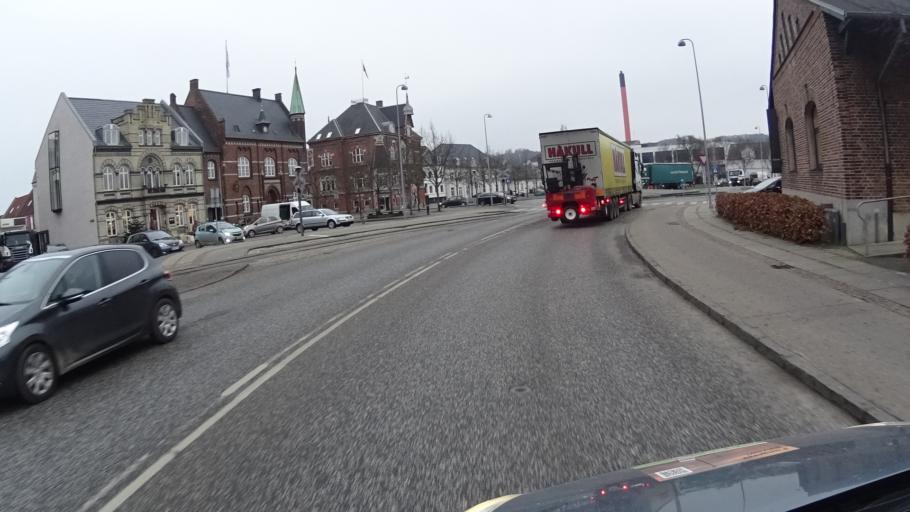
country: DK
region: South Denmark
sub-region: Vejle Kommune
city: Vejle
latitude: 55.7064
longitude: 9.5420
